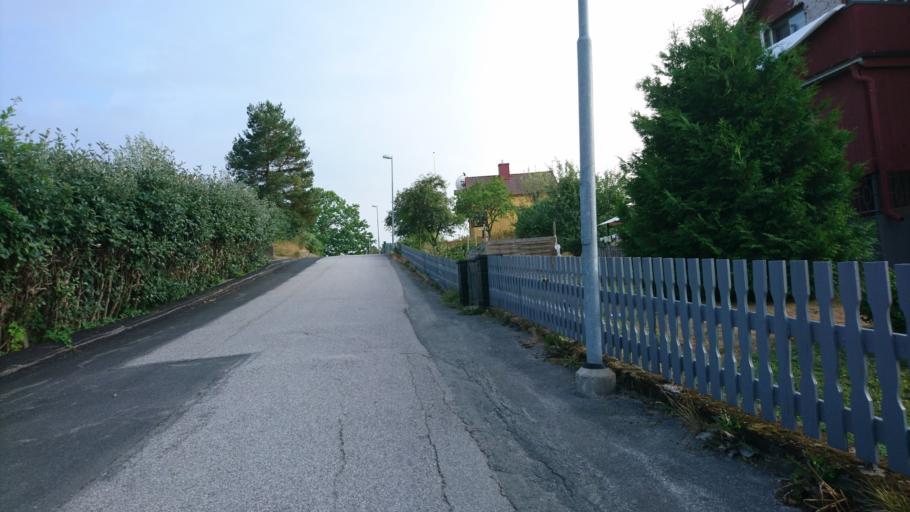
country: SE
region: Kalmar
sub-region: Vasterviks Kommun
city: Vaestervik
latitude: 57.7217
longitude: 16.5290
